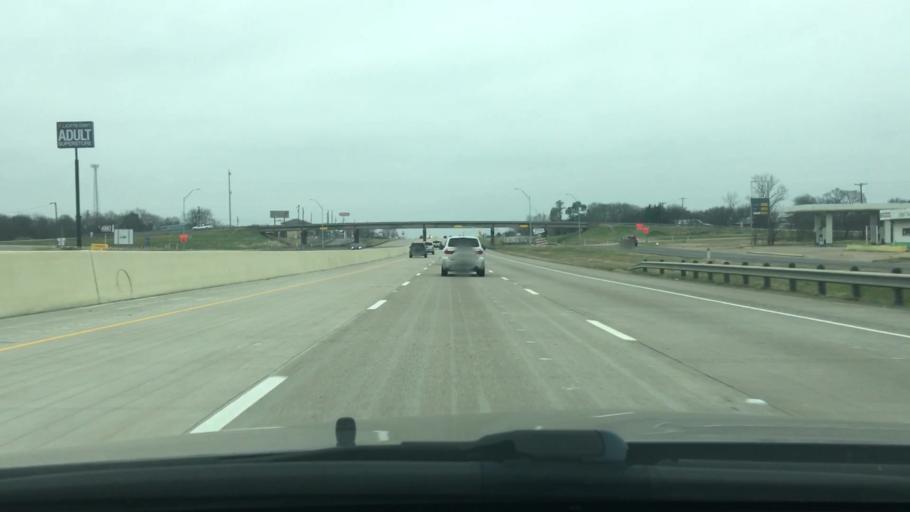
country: US
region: Texas
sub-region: Navarro County
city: Corsicana
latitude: 32.0109
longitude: -96.4350
